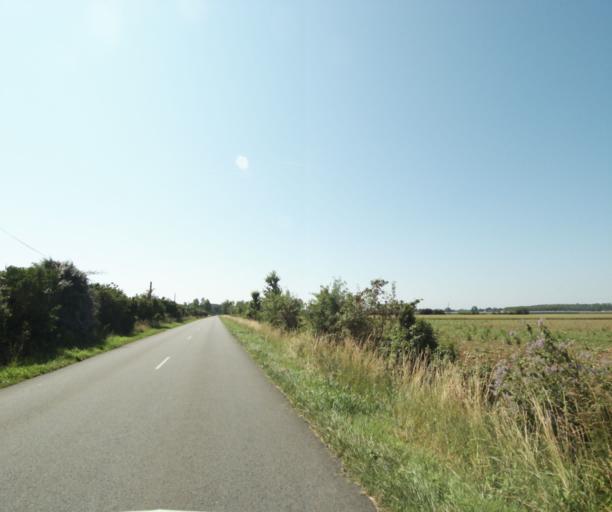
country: FR
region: Midi-Pyrenees
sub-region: Departement du Tarn-et-Garonne
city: Montbeton
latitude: 44.0524
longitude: 1.2887
